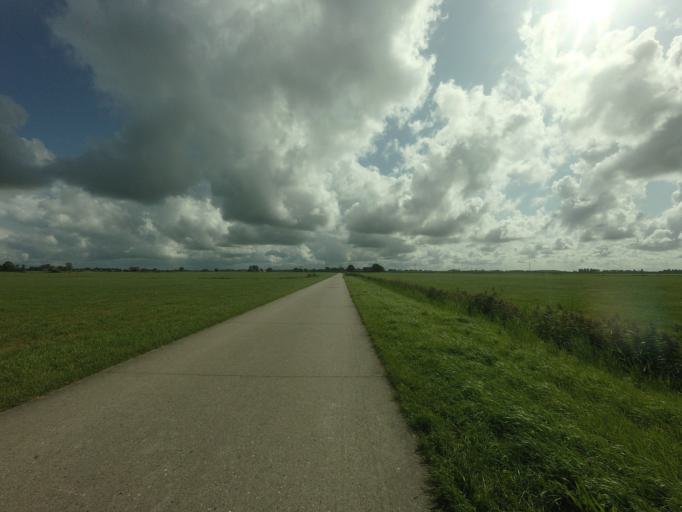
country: NL
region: Friesland
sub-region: Sudwest Fryslan
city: Scharnegoutum
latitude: 53.0695
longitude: 5.6382
